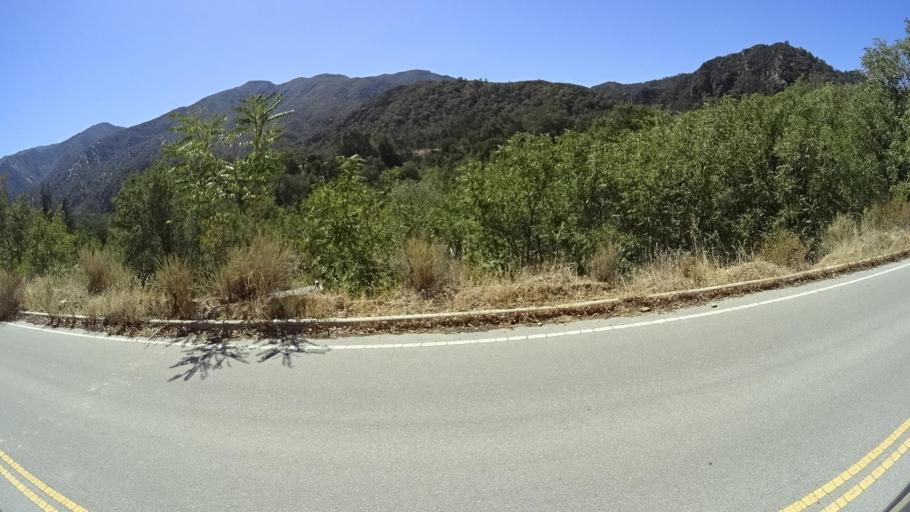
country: US
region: California
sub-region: Monterey County
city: Soledad
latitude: 36.2368
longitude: -121.4710
